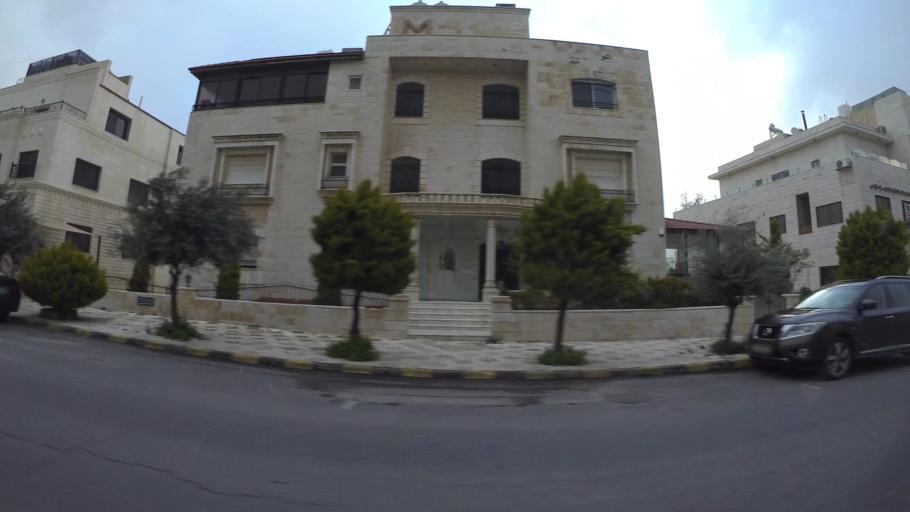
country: JO
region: Amman
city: Amman
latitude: 31.9517
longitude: 35.8907
